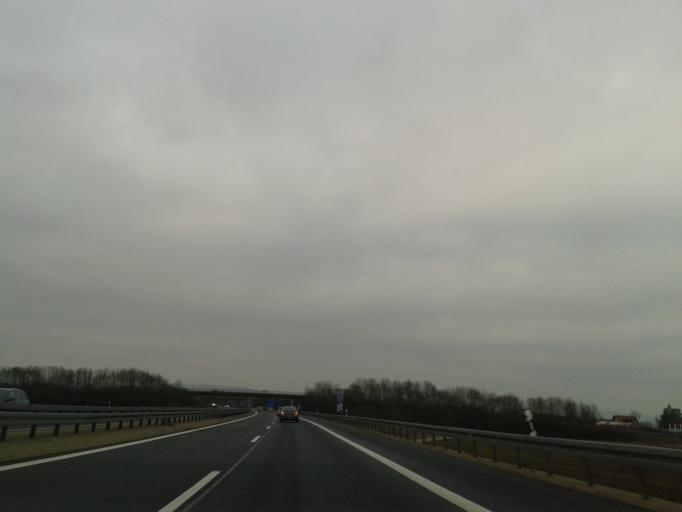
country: DE
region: Bavaria
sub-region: Upper Franconia
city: Bischberg
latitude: 49.9173
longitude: 10.8527
